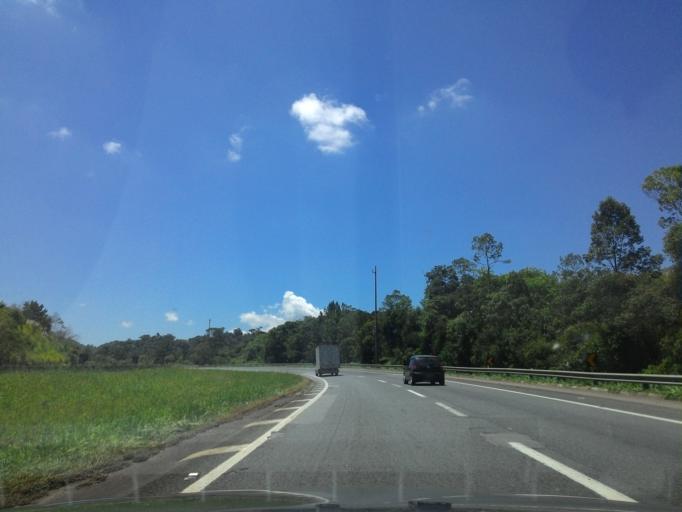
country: BR
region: Parana
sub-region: Antonina
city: Antonina
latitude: -25.0743
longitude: -48.5879
